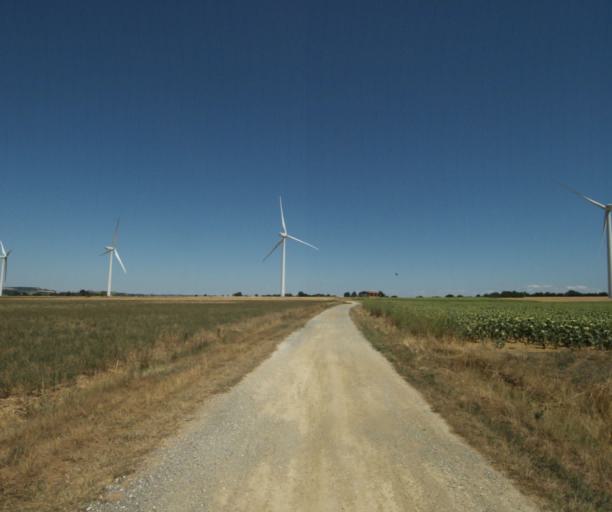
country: FR
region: Midi-Pyrenees
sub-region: Departement de la Haute-Garonne
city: Saint-Felix-Lauragais
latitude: 43.4619
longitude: 1.9163
